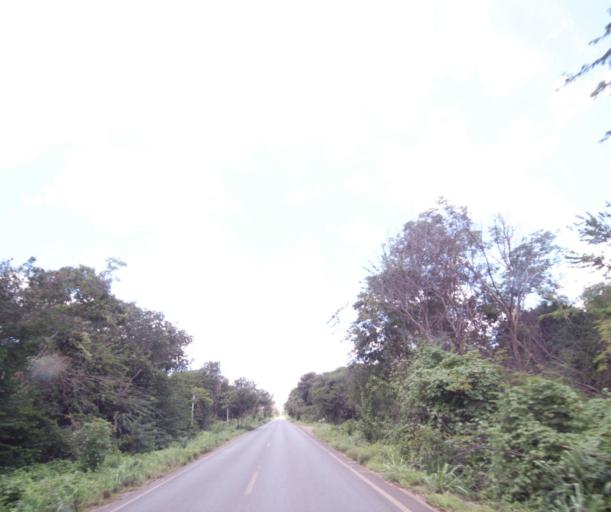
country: BR
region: Bahia
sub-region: Bom Jesus Da Lapa
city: Bom Jesus da Lapa
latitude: -13.2638
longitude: -43.5613
